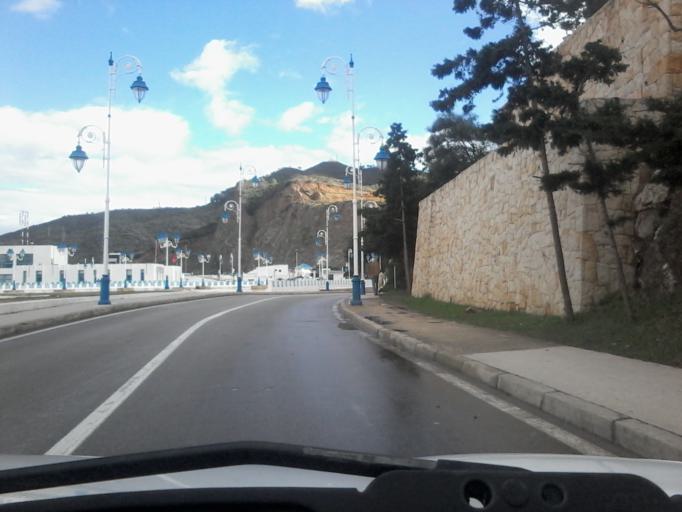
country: MA
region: Tanger-Tetouan
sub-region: Tetouan
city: Martil
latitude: 35.6820
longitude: -5.3150
